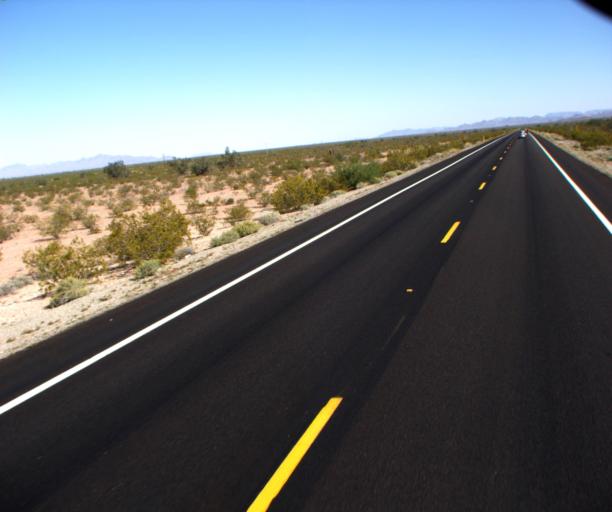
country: US
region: Arizona
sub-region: La Paz County
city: Quartzsite
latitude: 33.2858
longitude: -114.2284
